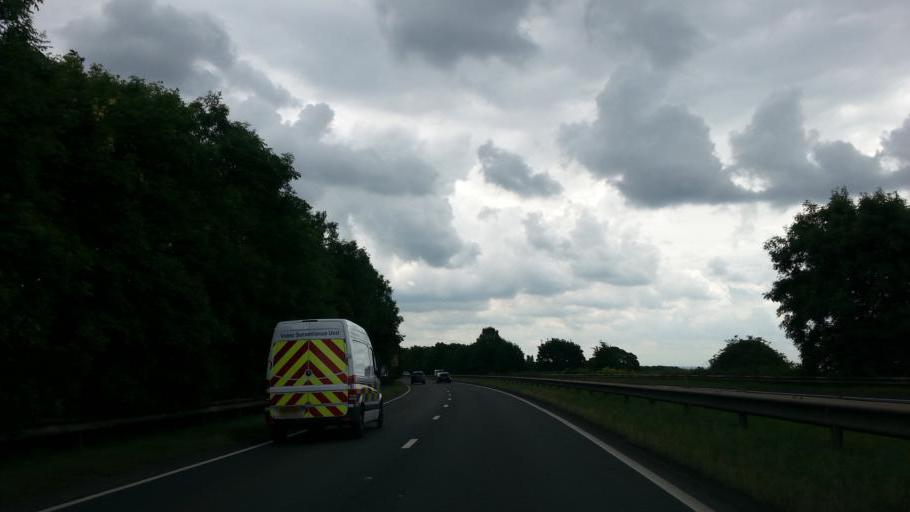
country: GB
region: England
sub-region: City and Borough of Birmingham
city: Sutton Coldfield
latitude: 52.5962
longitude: -1.7934
